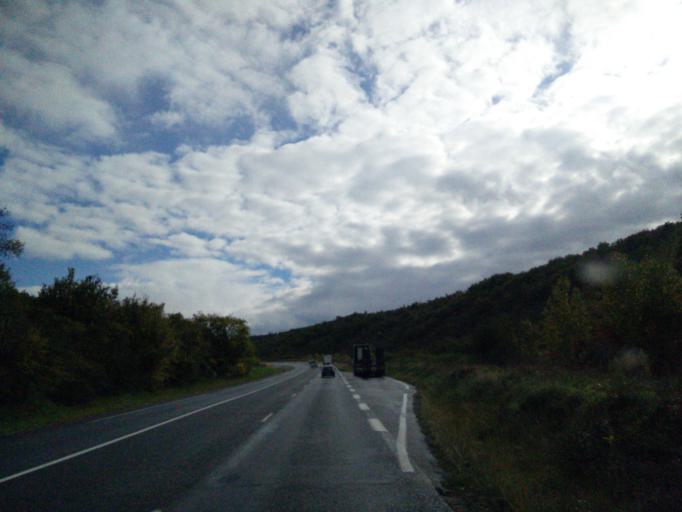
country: FR
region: Midi-Pyrenees
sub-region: Departement du Lot
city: Cahors
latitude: 44.4542
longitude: 1.4125
